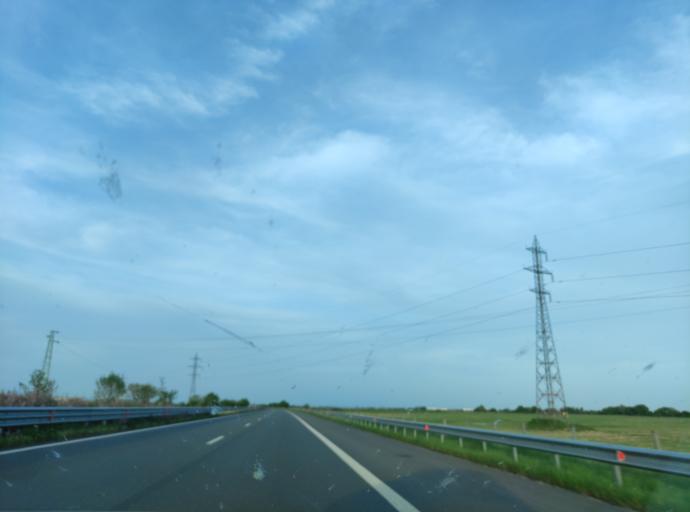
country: BG
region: Plovdiv
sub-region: Obshtina Rakovski
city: Rakovski
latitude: 42.2135
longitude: 24.9826
